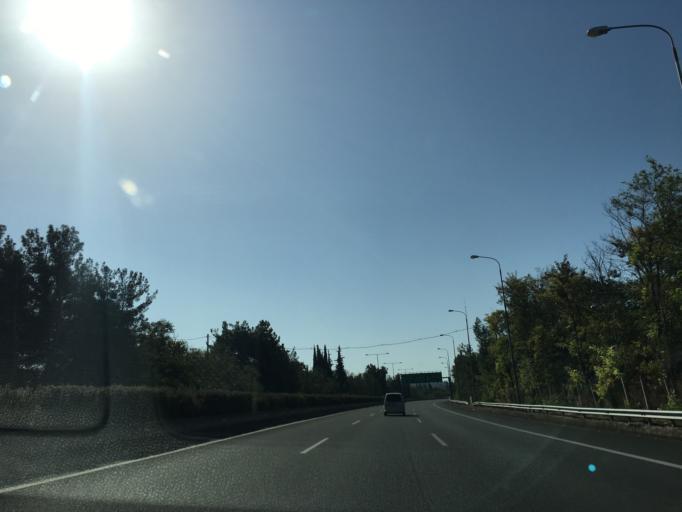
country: GR
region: Central Macedonia
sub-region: Nomos Pierias
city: Aiginio
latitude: 40.4679
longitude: 22.5754
